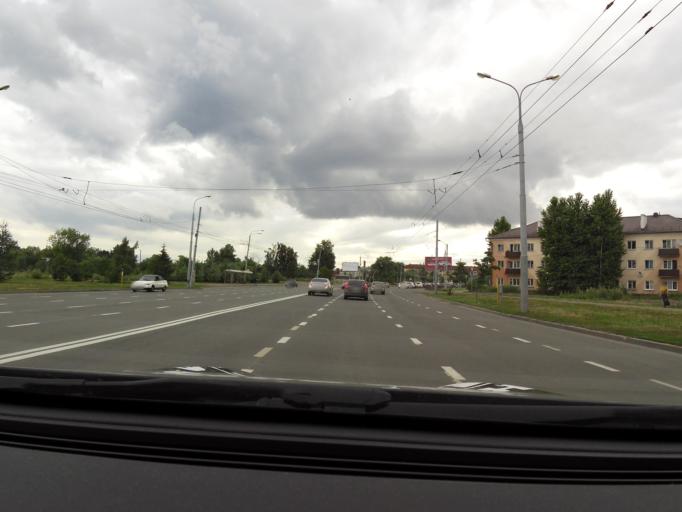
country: RU
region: Tatarstan
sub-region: Gorod Kazan'
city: Kazan
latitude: 55.8133
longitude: 49.0796
